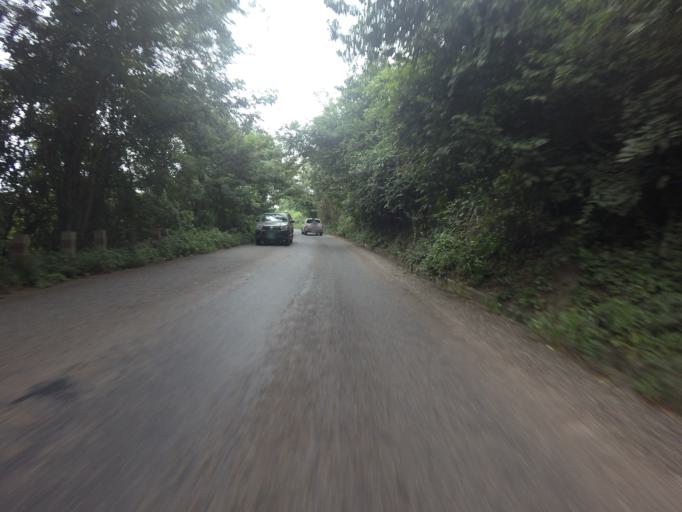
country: GH
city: Akropong
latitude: 5.9591
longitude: -0.1195
